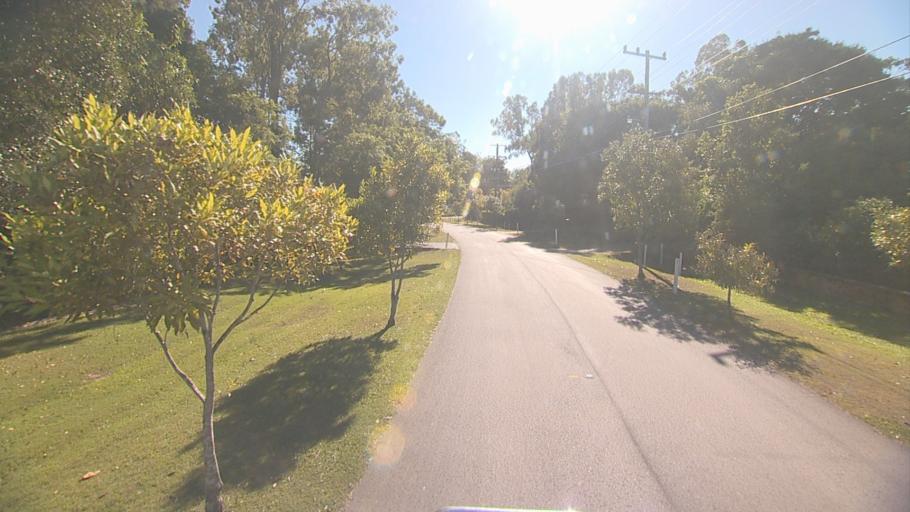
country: AU
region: Queensland
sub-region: Brisbane
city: Forest Lake
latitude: -27.6633
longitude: 153.0029
